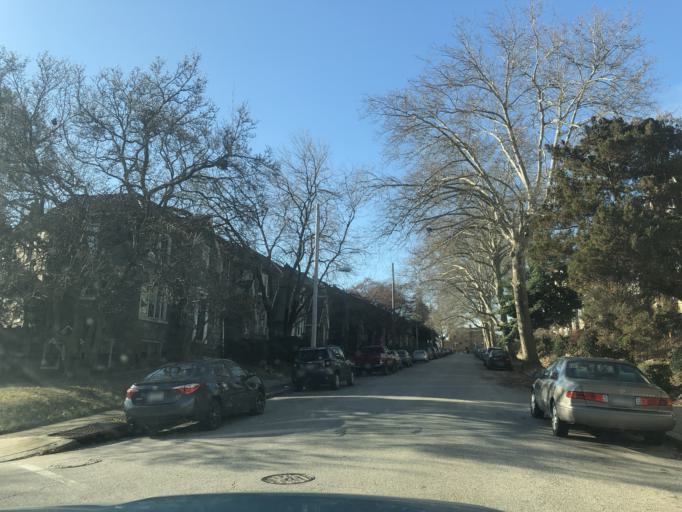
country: US
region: Pennsylvania
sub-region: Montgomery County
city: Bala-Cynwyd
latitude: 39.9898
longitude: -75.2379
